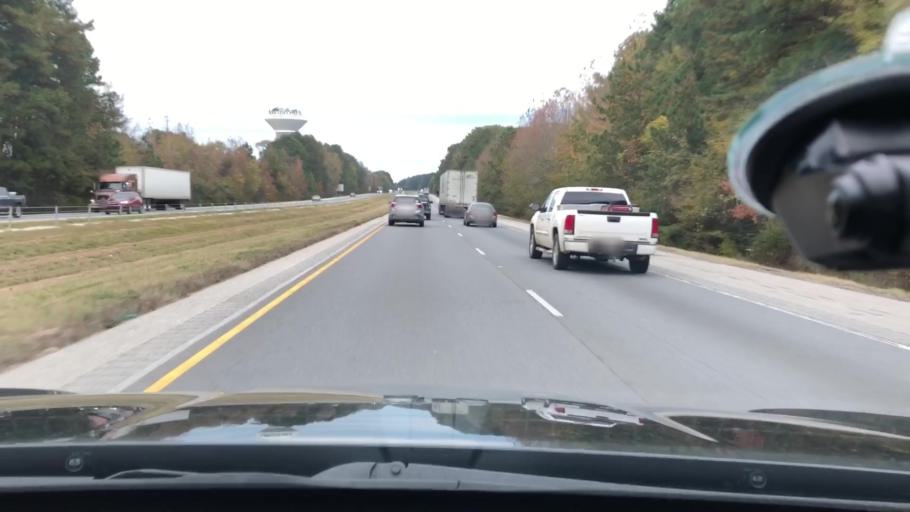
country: US
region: Arkansas
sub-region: Clark County
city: Arkadelphia
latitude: 34.1298
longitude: -93.0867
